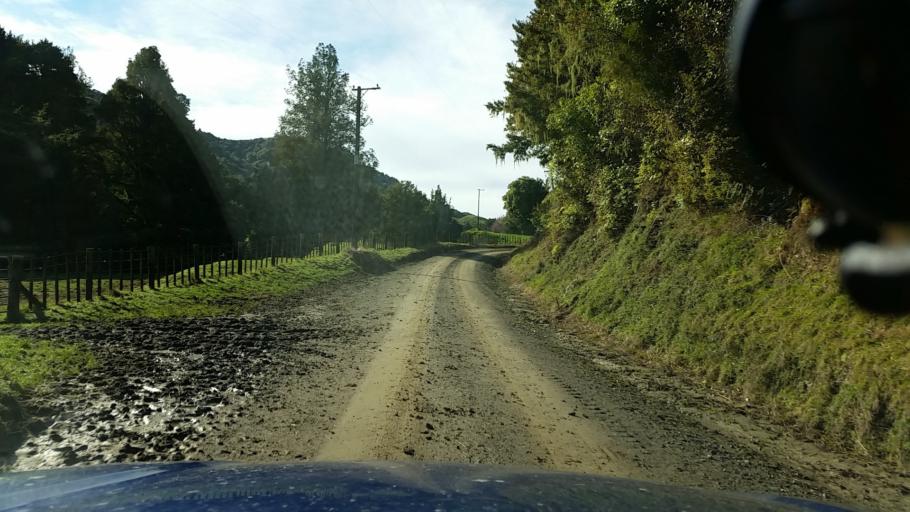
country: NZ
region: Taranaki
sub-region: New Plymouth District
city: Waitara
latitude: -39.0511
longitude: 174.7612
